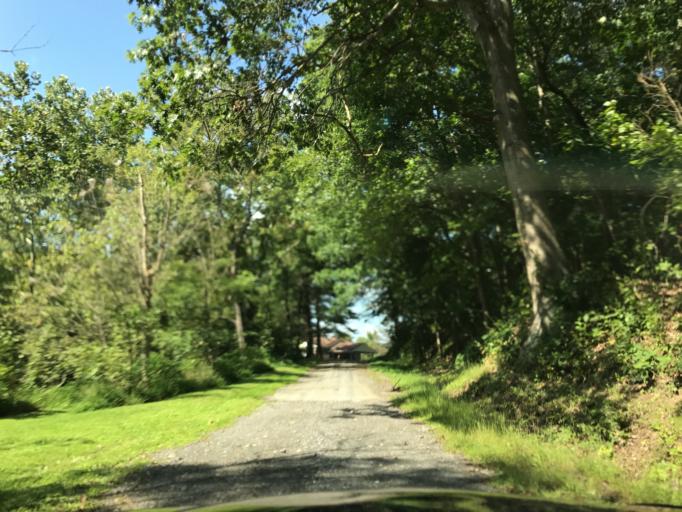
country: US
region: Pennsylvania
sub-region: York County
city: New Freedom
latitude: 39.6444
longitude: -76.6606
